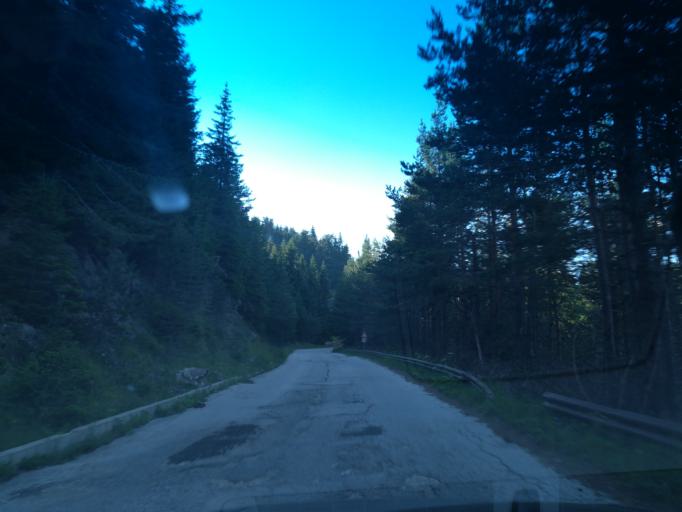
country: BG
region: Smolyan
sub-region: Obshtina Chepelare
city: Chepelare
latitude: 41.6908
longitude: 24.7571
